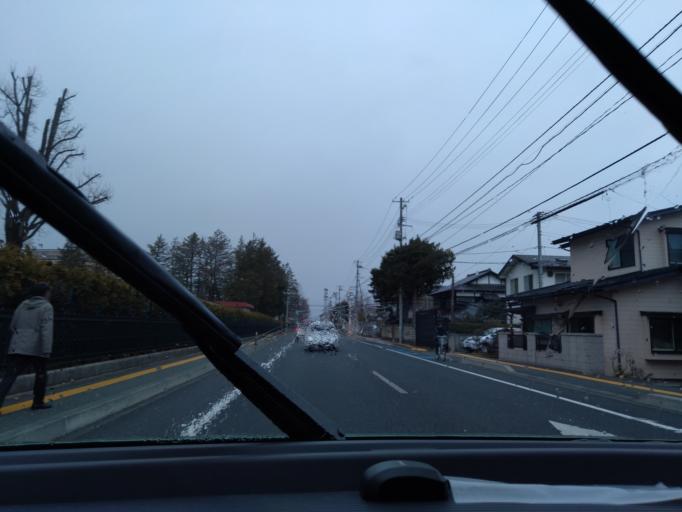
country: JP
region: Iwate
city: Morioka-shi
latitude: 39.7141
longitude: 141.1403
